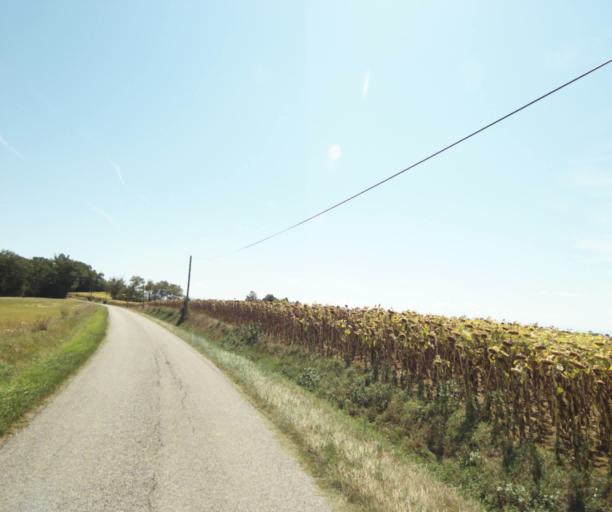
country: FR
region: Midi-Pyrenees
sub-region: Departement de l'Ariege
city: Lezat-sur-Leze
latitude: 43.2814
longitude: 1.3045
